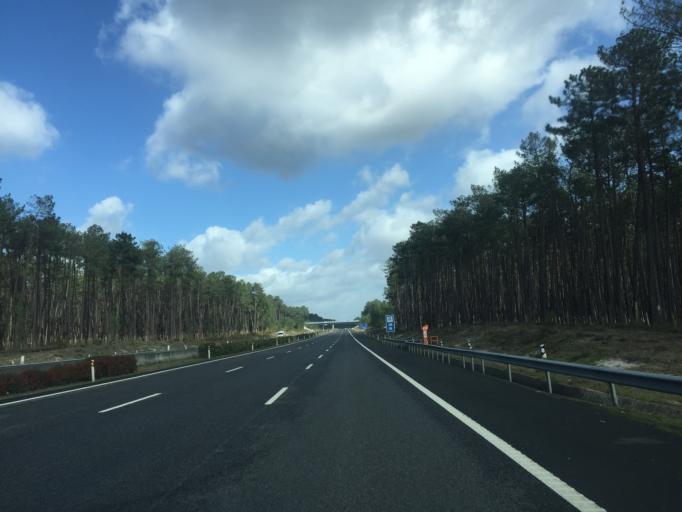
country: PT
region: Leiria
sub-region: Alcobaca
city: Pataias
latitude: 39.6506
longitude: -8.9632
